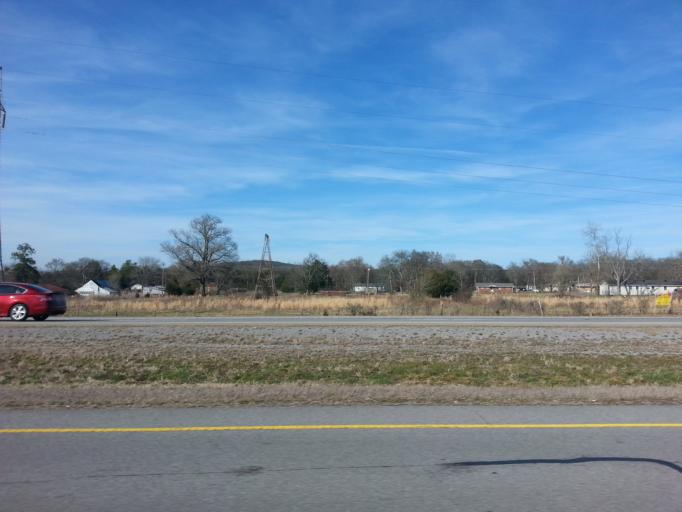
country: US
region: Tennessee
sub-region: Rutherford County
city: Murfreesboro
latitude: 35.8193
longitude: -86.2398
